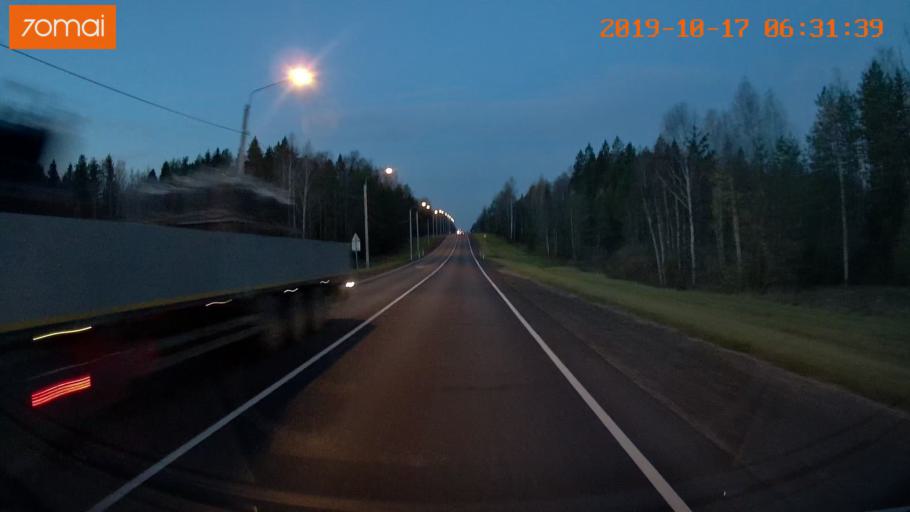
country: RU
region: Ivanovo
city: Novoye Leushino
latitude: 56.7261
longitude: 40.6934
